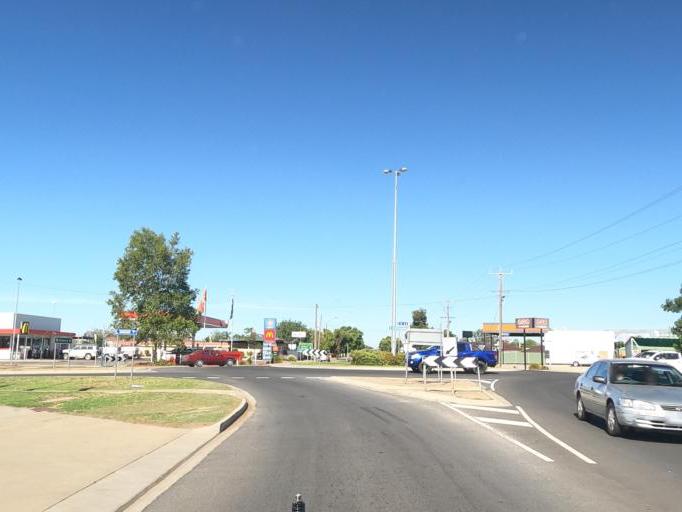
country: AU
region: Victoria
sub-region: Moira
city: Yarrawonga
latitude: -36.0176
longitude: 146.0051
